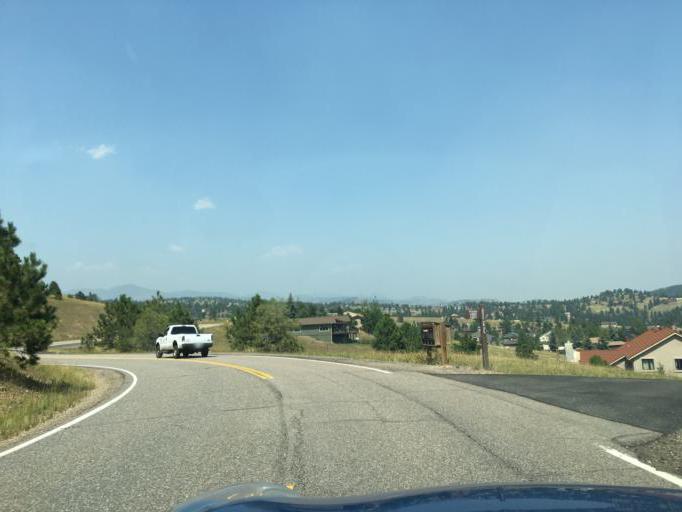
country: US
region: Colorado
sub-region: Jefferson County
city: Genesee
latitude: 39.6979
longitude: -105.2713
